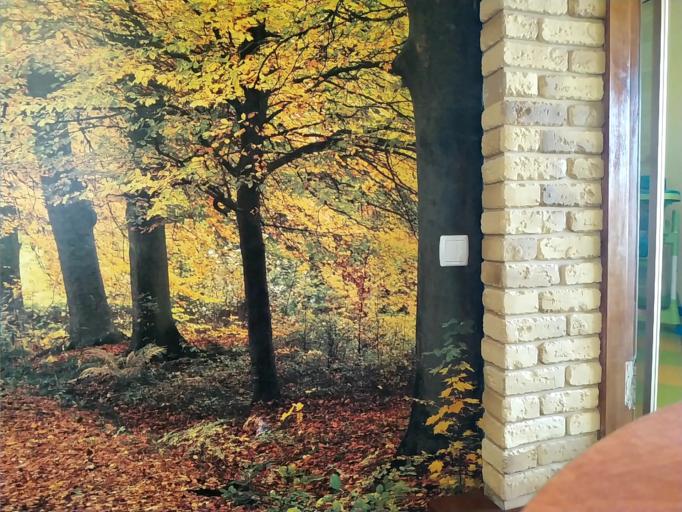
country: RU
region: Tverskaya
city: Maksatikha
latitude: 57.6179
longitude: 35.8965
